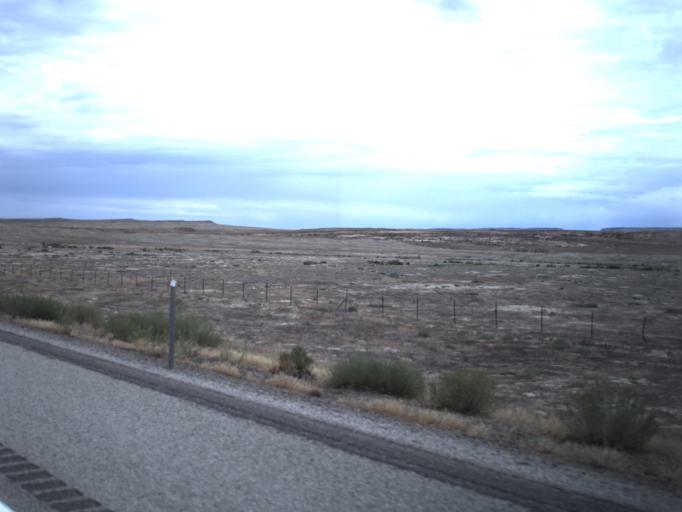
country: US
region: Utah
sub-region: Grand County
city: Moab
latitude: 39.0118
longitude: -109.3063
